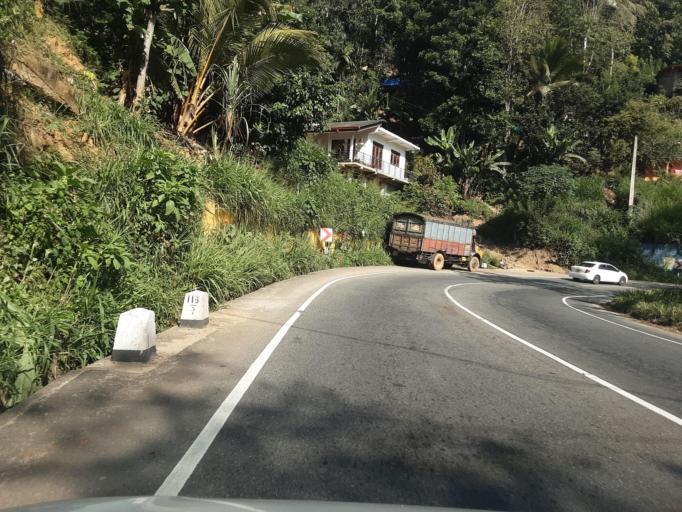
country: LK
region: Uva
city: Badulla
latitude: 6.9760
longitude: 81.0446
